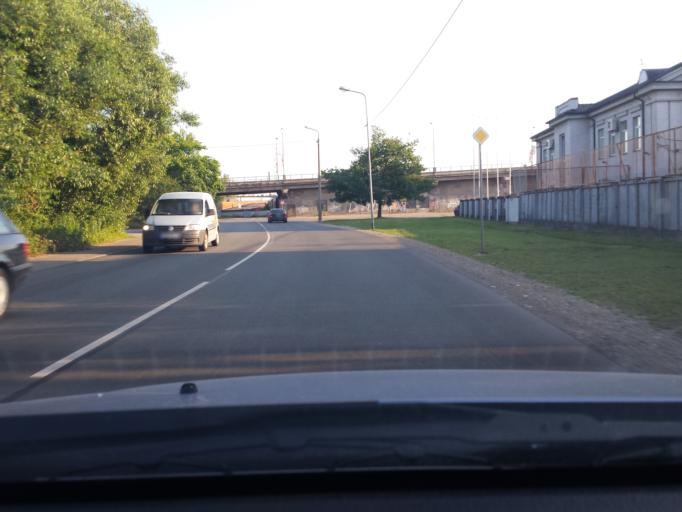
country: LV
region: Riga
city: Riga
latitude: 56.9533
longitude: 24.1633
